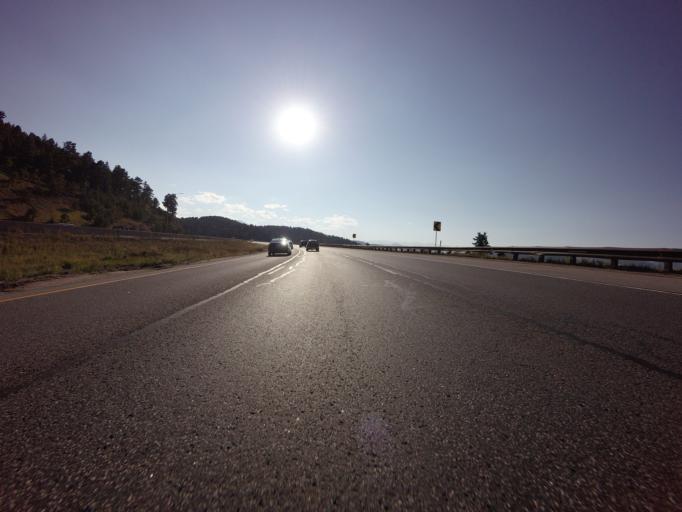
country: US
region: Colorado
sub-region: Jefferson County
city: Genesee
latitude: 39.7144
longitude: -105.3112
